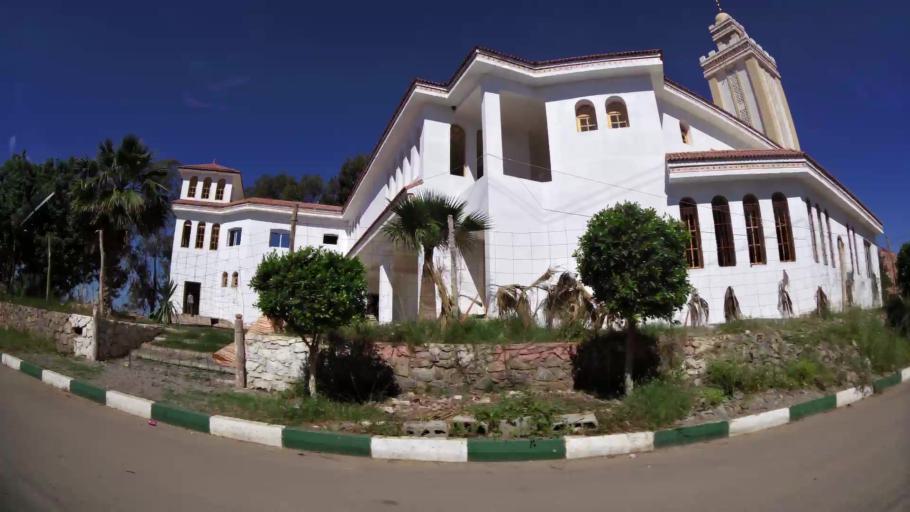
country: MA
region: Oriental
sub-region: Berkane-Taourirt
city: Berkane
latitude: 34.9404
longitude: -2.3249
